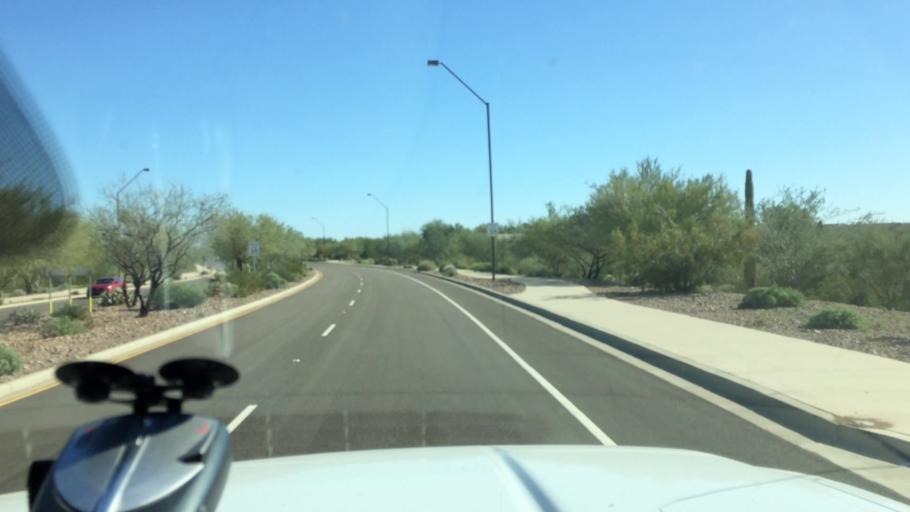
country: US
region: Arizona
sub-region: Maricopa County
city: Anthem
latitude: 33.8516
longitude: -112.1021
